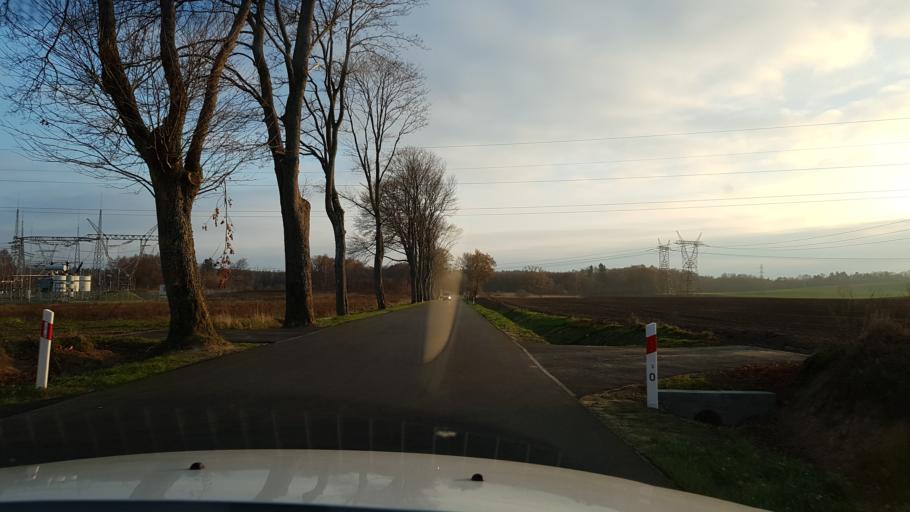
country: PL
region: West Pomeranian Voivodeship
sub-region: Koszalin
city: Koszalin
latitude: 54.1290
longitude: 16.0882
